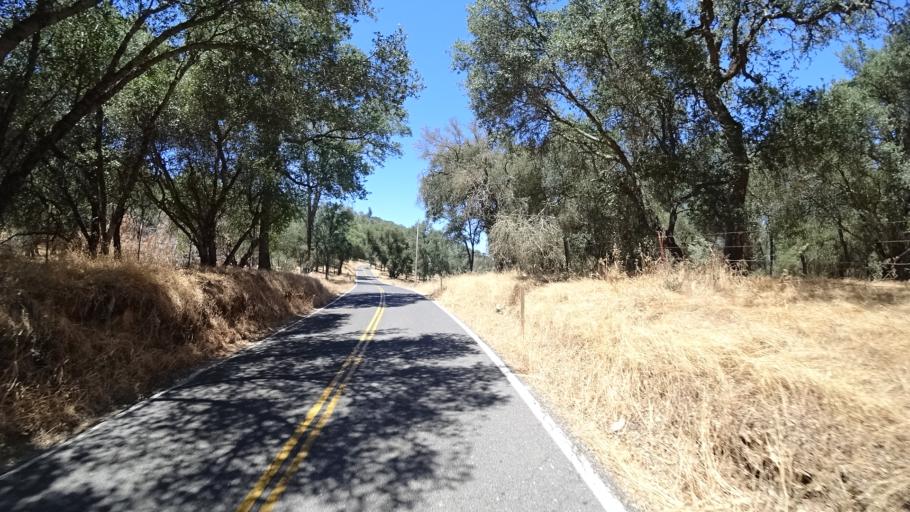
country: US
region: California
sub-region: Calaveras County
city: San Andreas
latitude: 38.1289
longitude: -120.6625
